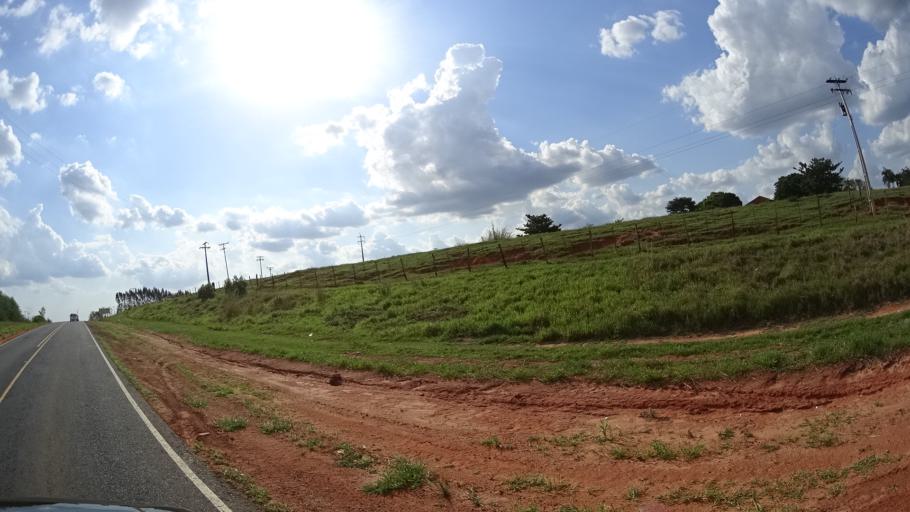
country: BR
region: Sao Paulo
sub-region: Urupes
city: Urupes
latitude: -21.1896
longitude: -49.3028
